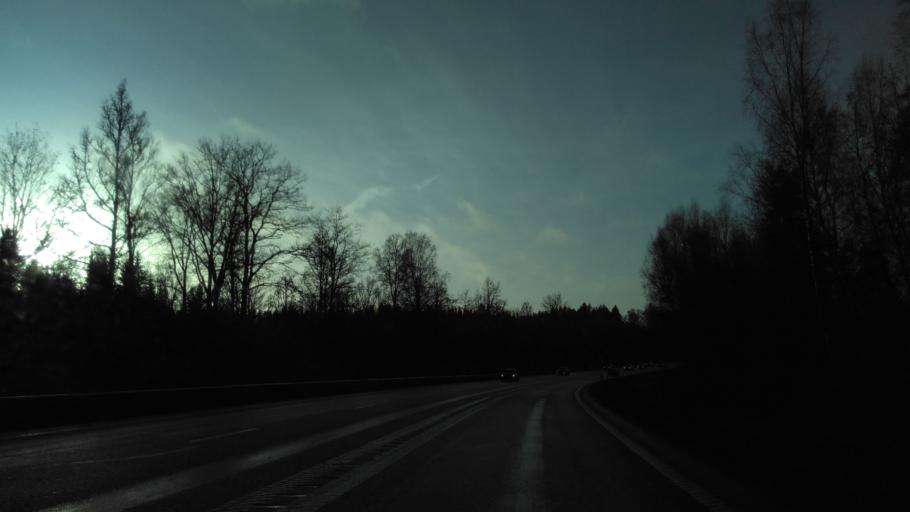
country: SE
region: Vaestra Goetaland
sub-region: Vargarda Kommun
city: Vargarda
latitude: 58.0103
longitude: 12.7714
